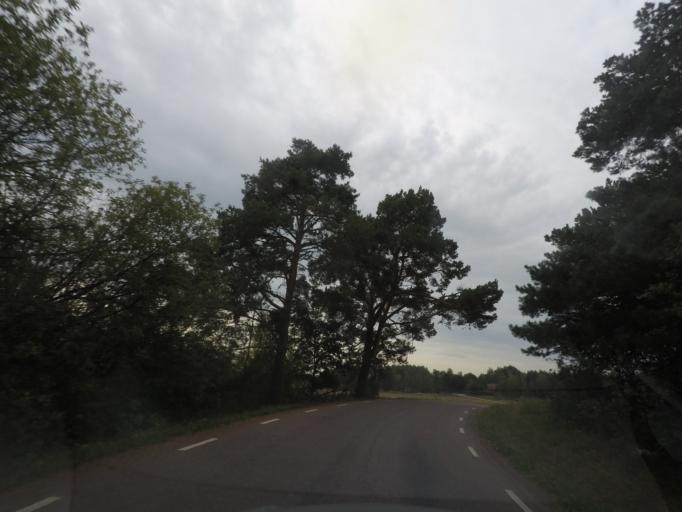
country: SE
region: Vaestmanland
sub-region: Hallstahammars Kommun
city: Kolback
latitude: 59.5173
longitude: 16.1885
